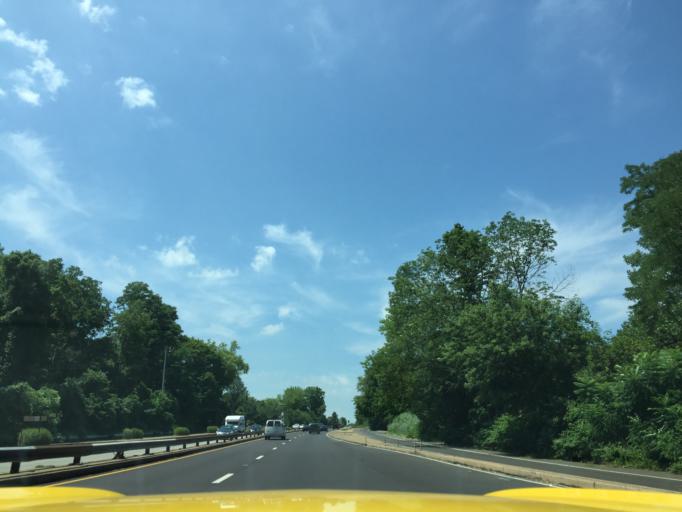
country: US
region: Pennsylvania
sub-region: Bucks County
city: Langhorne Manor
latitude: 40.1657
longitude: -74.9258
